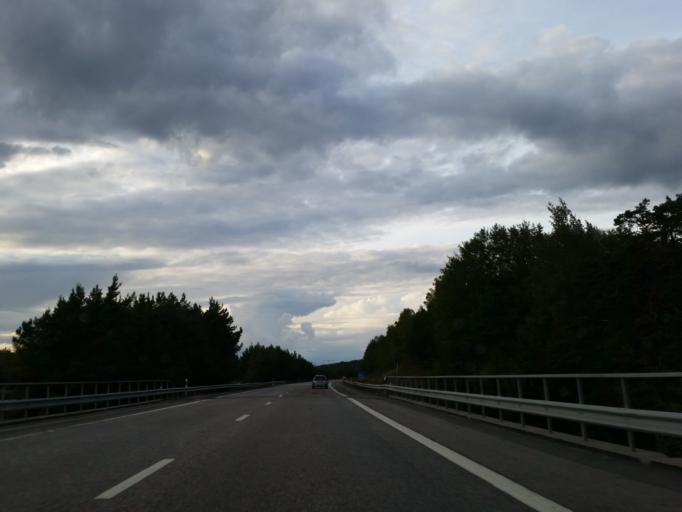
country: SE
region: Uppsala
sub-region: Knivsta Kommun
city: Knivsta
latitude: 59.7344
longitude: 17.8254
